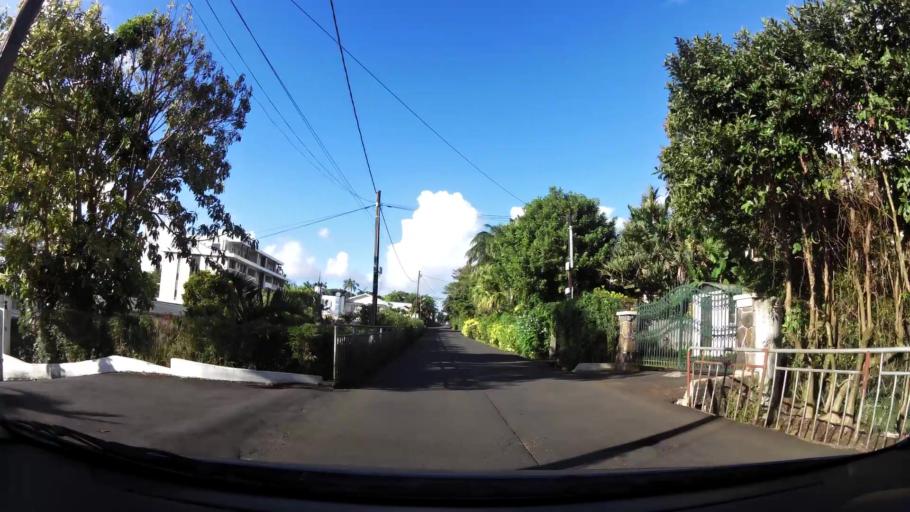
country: MU
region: Plaines Wilhems
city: Curepipe
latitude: -20.3133
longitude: 57.5037
